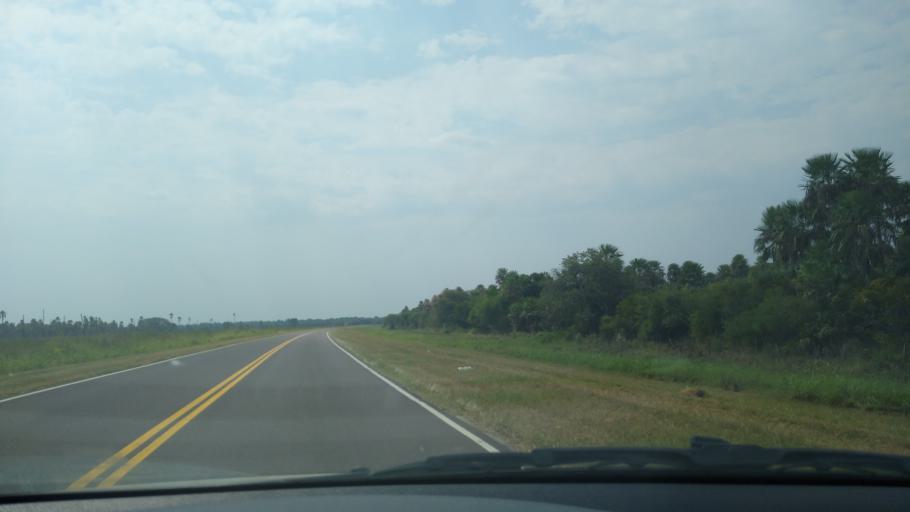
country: AR
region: Chaco
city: Margarita Belen
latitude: -27.0734
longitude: -58.9623
